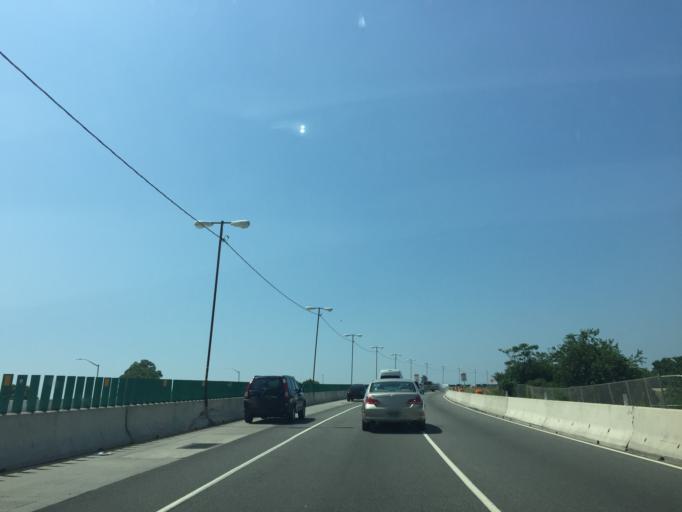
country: US
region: New York
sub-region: Kings County
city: Brooklyn
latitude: 40.5889
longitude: -73.9091
